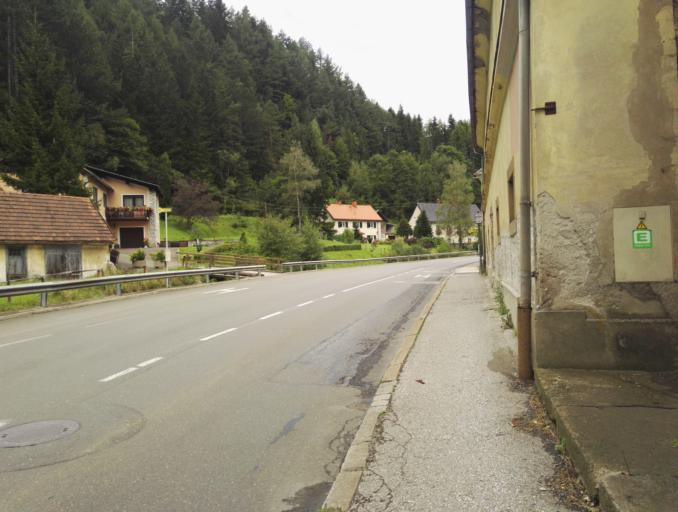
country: AT
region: Styria
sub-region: Politischer Bezirk Leoben
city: Vordernberg
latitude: 47.4827
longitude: 14.9891
